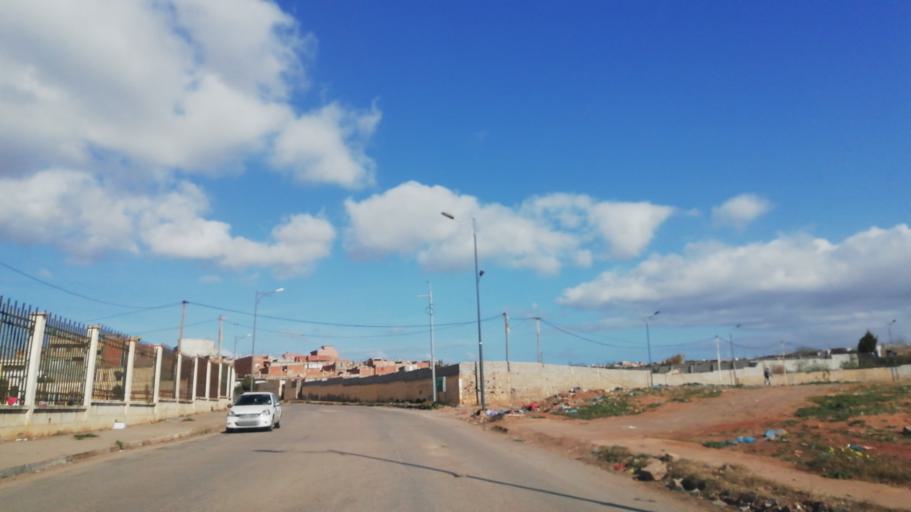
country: DZ
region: Oran
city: Es Senia
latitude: 35.6323
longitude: -0.6617
